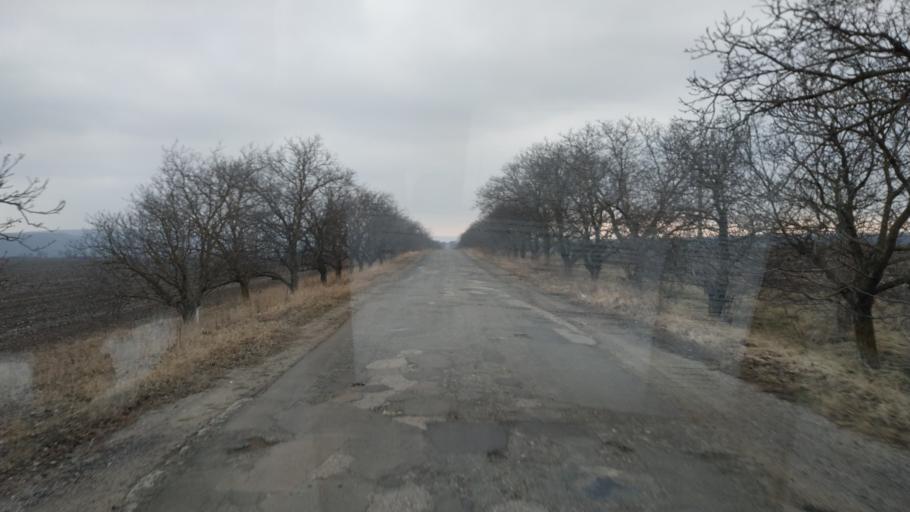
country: MD
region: Hincesti
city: Dancu
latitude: 46.8806
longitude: 28.2983
